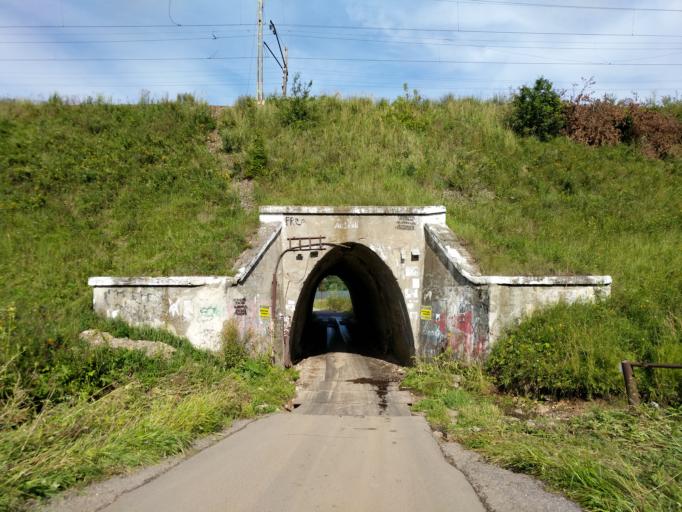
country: RU
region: Moskovskaya
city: Yermolino
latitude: 56.1395
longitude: 37.5065
